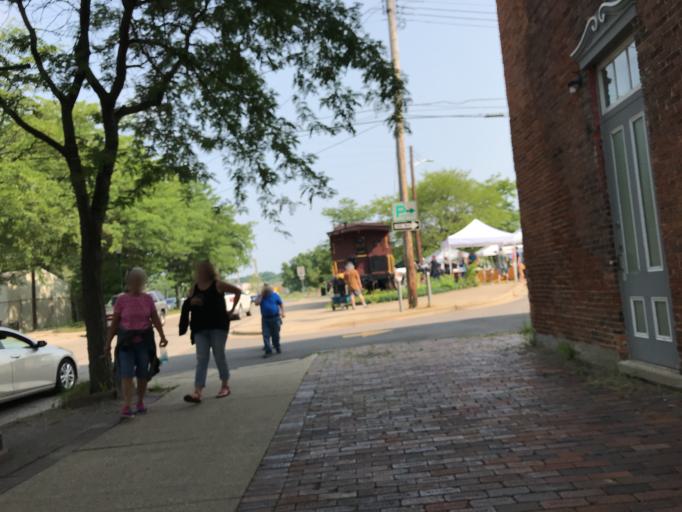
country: US
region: Michigan
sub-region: Washtenaw County
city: Ypsilanti
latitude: 42.2462
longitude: -83.6104
